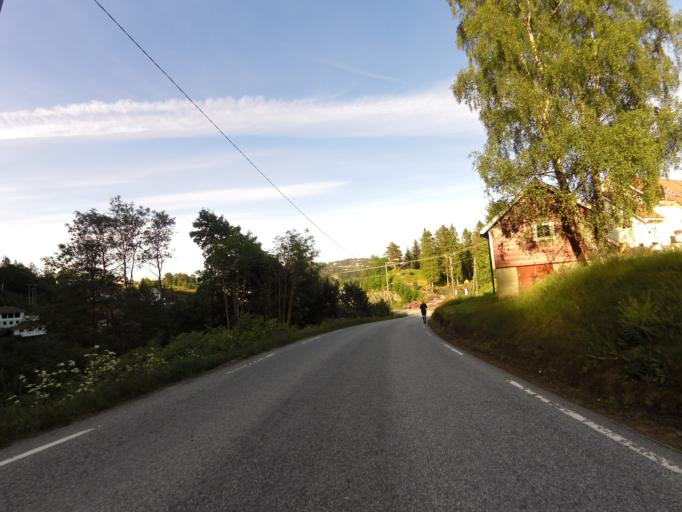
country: NO
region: Vest-Agder
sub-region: Flekkefjord
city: Flekkefjord
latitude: 58.2852
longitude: 6.6460
